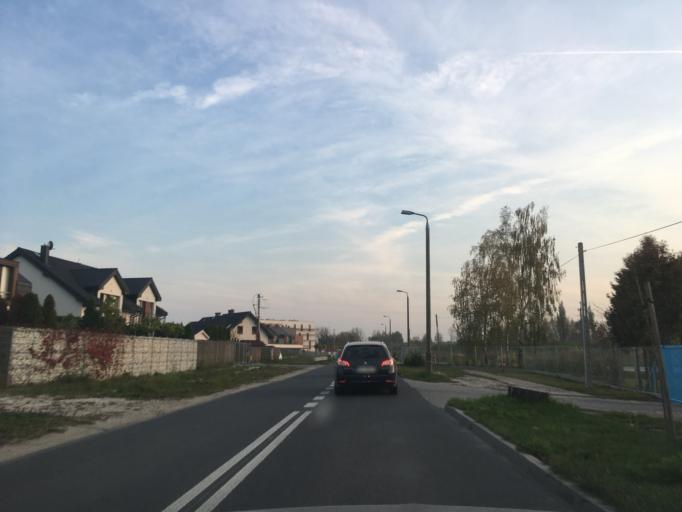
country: PL
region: Masovian Voivodeship
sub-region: Powiat piaseczynski
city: Lesznowola
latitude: 52.0740
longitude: 20.8917
